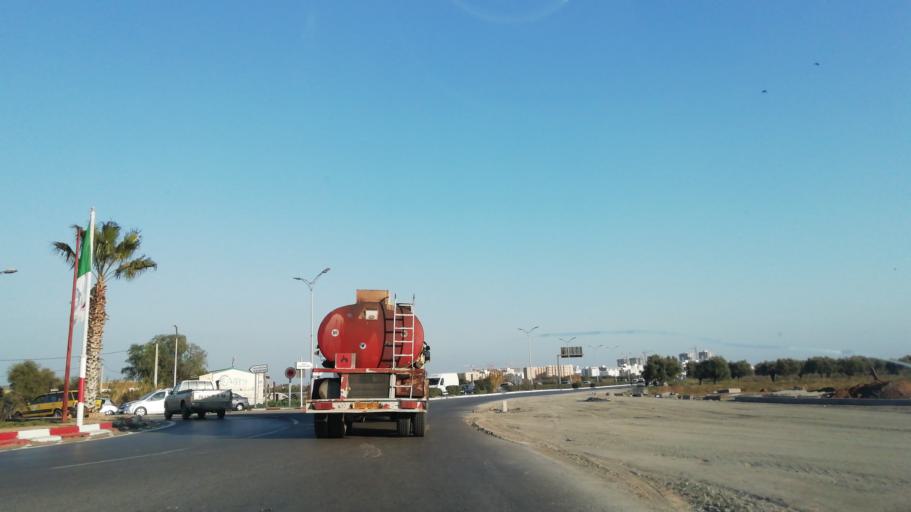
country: DZ
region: Sidi Bel Abbes
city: Sidi Bel Abbes
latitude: 35.1816
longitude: -0.6585
